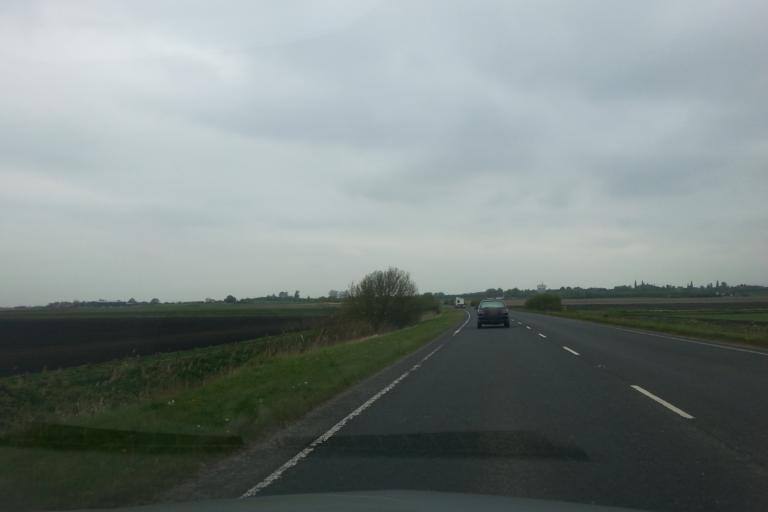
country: GB
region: England
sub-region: Cambridgeshire
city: Littleport
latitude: 52.4350
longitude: 0.2812
